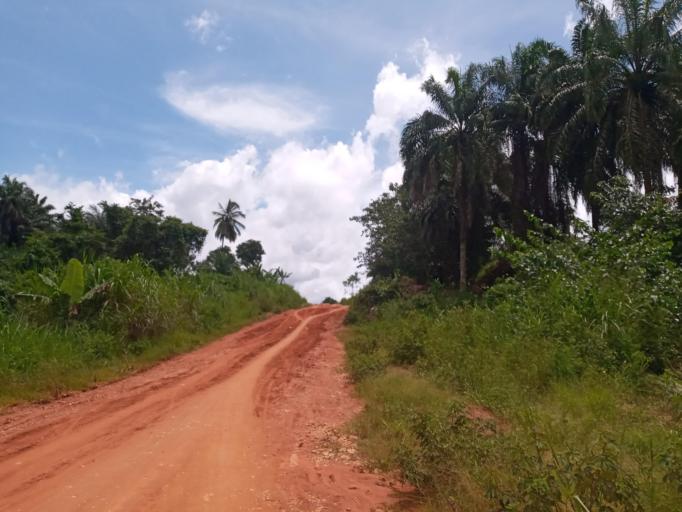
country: SL
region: Eastern Province
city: Koidu
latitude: 8.6437
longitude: -10.9107
